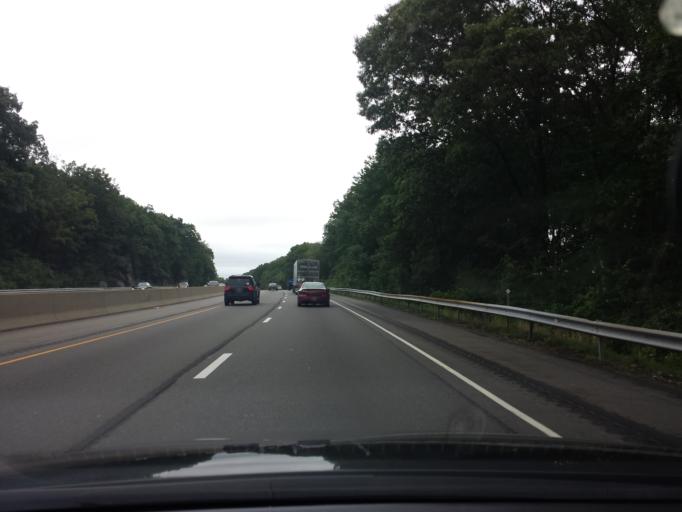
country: US
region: Connecticut
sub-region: Middlesex County
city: Clinton
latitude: 41.2882
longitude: -72.5573
